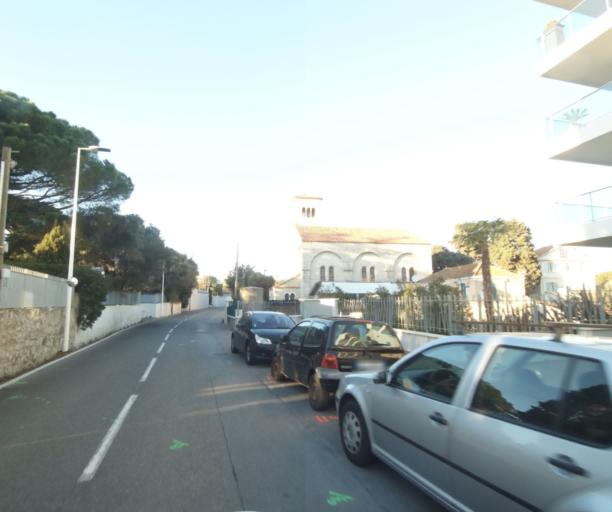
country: FR
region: Provence-Alpes-Cote d'Azur
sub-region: Departement des Alpes-Maritimes
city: Antibes
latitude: 43.5538
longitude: 7.1287
